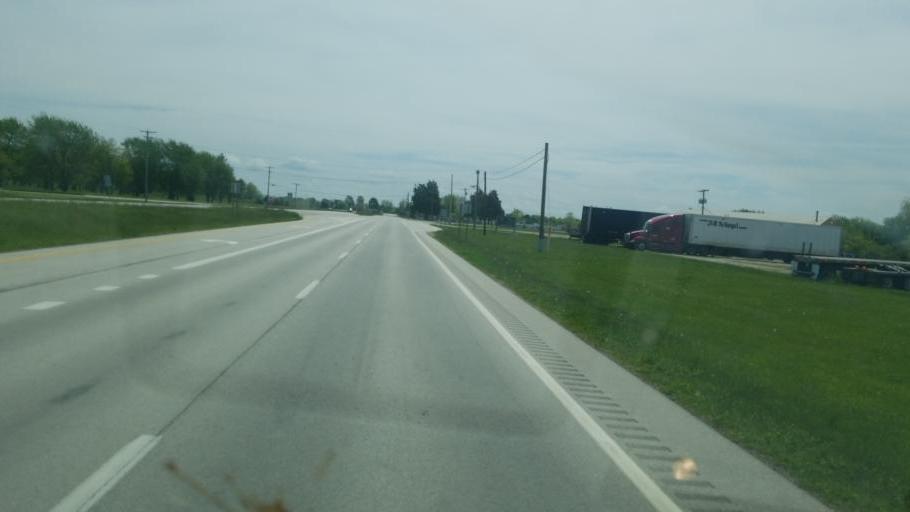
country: US
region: Ohio
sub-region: Ottawa County
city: Port Clinton
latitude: 41.5390
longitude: -83.0365
